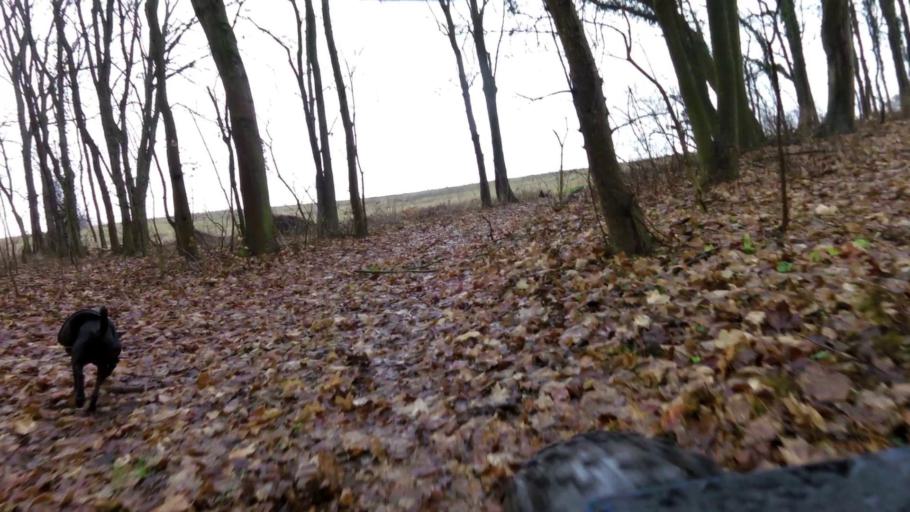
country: PL
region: Lubusz
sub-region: Powiat gorzowski
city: Kostrzyn nad Odra
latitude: 52.6227
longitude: 14.7005
